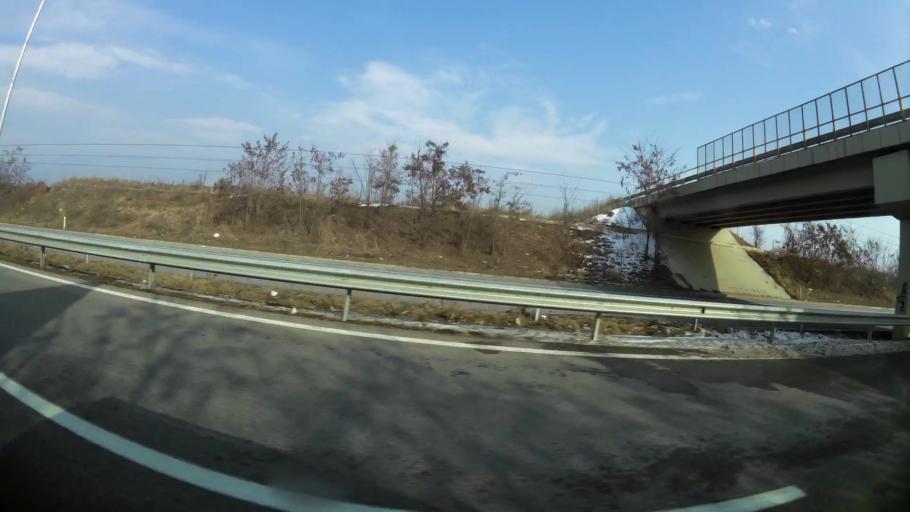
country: MK
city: Creshevo
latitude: 42.0313
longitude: 21.5278
